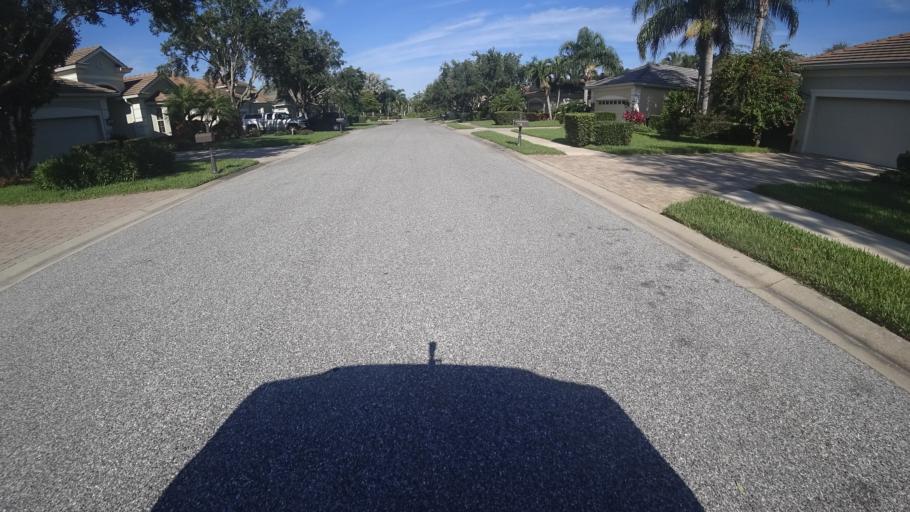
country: US
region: Florida
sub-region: Manatee County
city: West Bradenton
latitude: 27.5174
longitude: -82.6474
